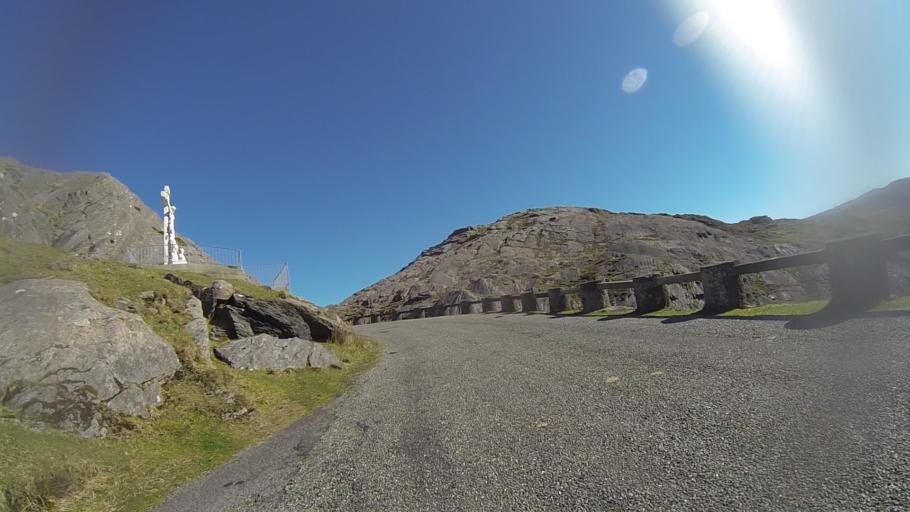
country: IE
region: Munster
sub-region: Ciarrai
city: Kenmare
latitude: 51.7212
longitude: -9.7566
